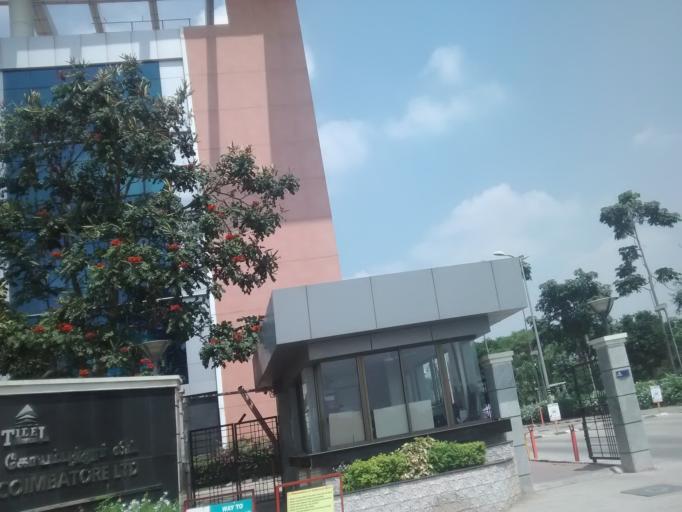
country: IN
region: Tamil Nadu
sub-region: Coimbatore
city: Singanallur
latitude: 11.0308
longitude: 77.0194
